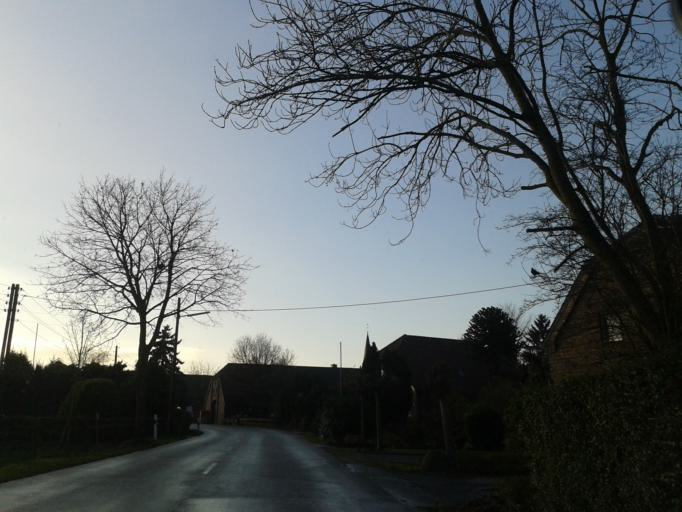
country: DE
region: North Rhine-Westphalia
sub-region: Regierungsbezirk Dusseldorf
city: Xanten
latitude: 51.6906
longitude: 6.4361
